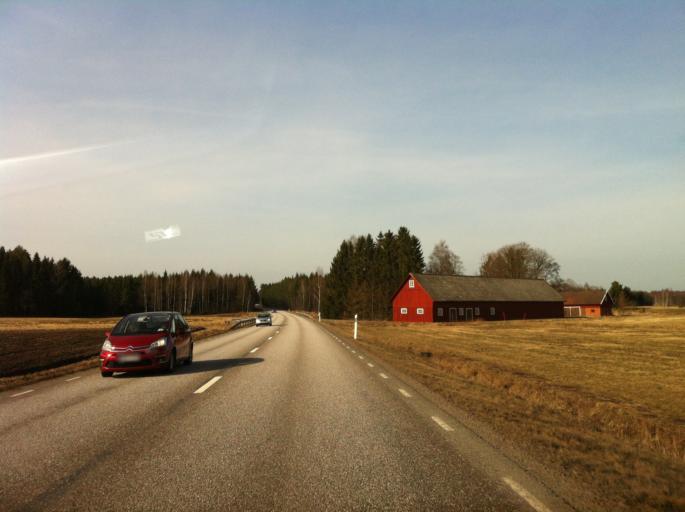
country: SE
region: Vaestra Goetaland
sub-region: Tidaholms Kommun
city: Tidaholm
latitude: 58.2066
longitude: 13.8786
